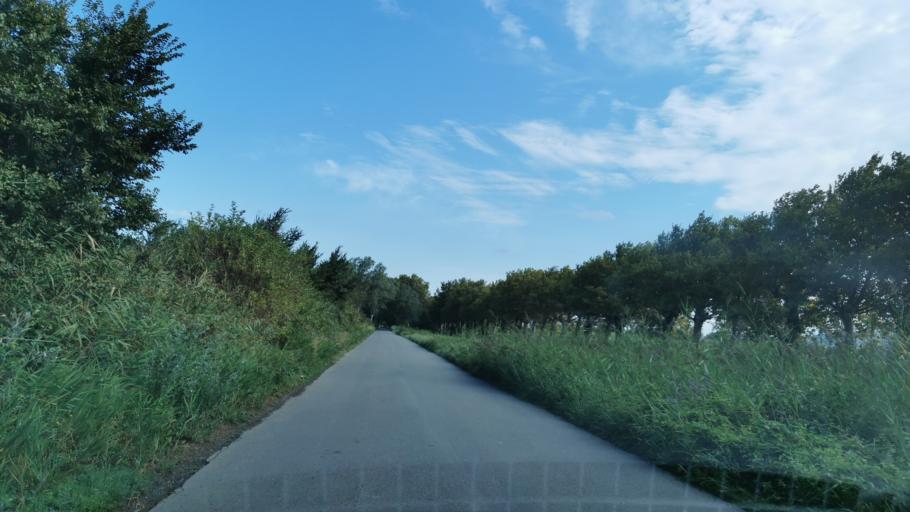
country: FR
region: Languedoc-Roussillon
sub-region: Departement de l'Aude
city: Gruissan
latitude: 43.1237
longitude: 3.0309
